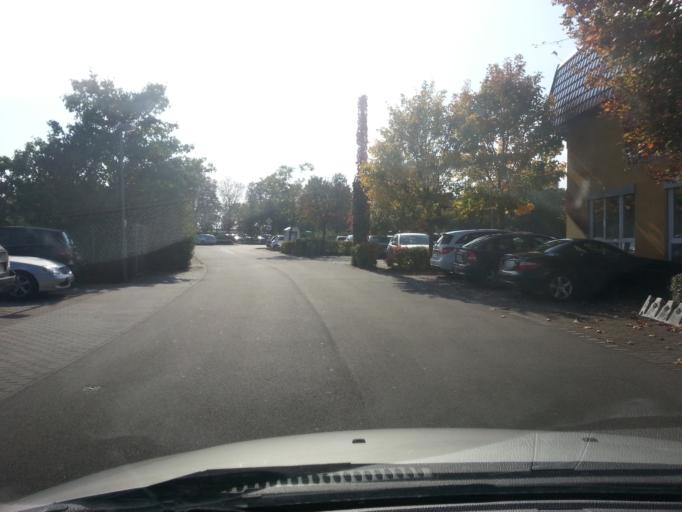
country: DE
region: Baden-Wuerttemberg
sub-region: Karlsruhe Region
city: Altlussheim
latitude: 49.3074
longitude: 8.4945
